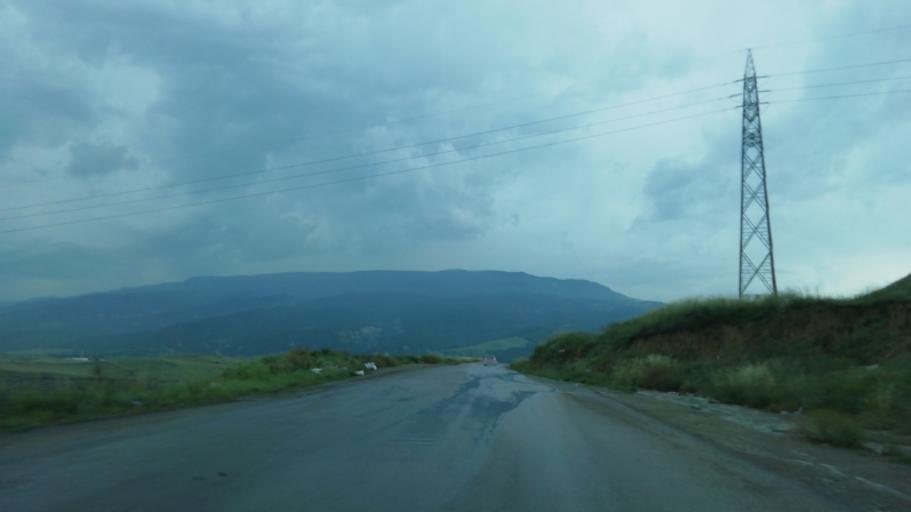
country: TR
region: Karabuk
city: Safranbolu
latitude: 41.2352
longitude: 32.6834
